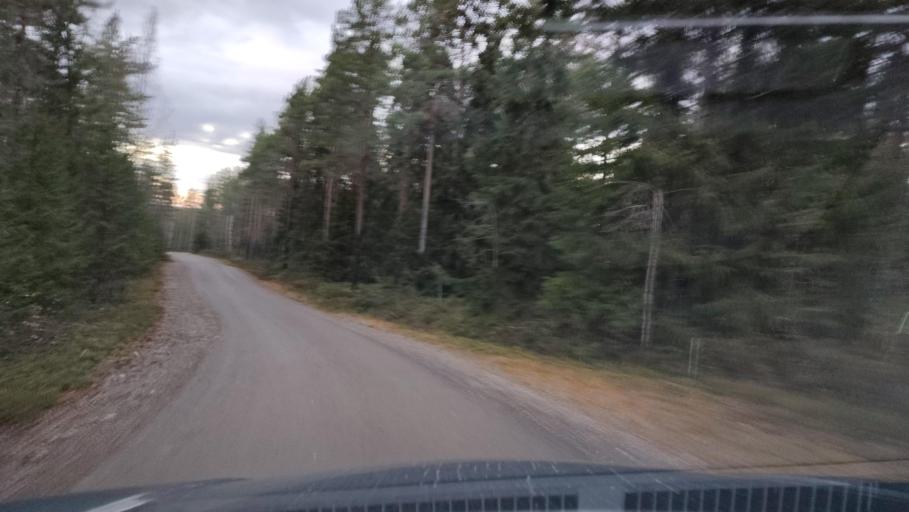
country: FI
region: Southern Ostrobothnia
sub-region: Suupohja
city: Karijoki
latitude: 62.2846
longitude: 21.6335
